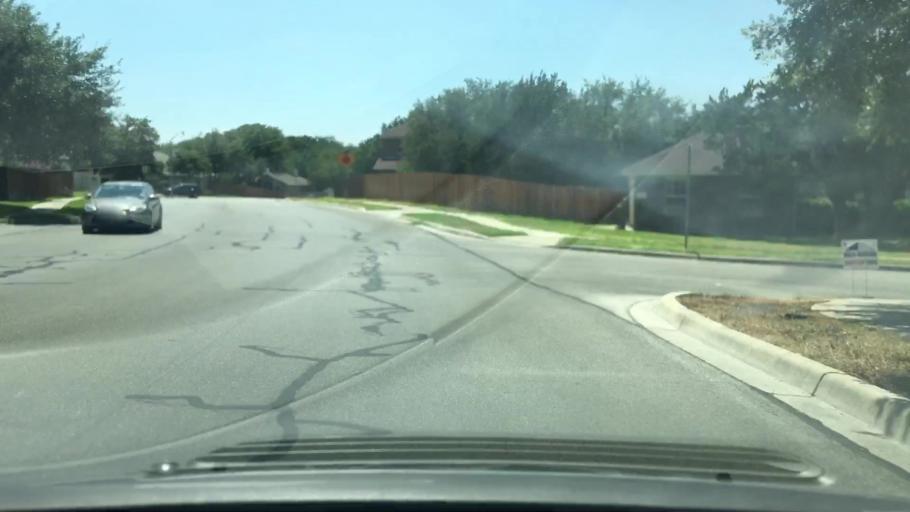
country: US
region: Texas
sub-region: Guadalupe County
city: Cibolo
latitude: 29.5814
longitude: -98.2532
